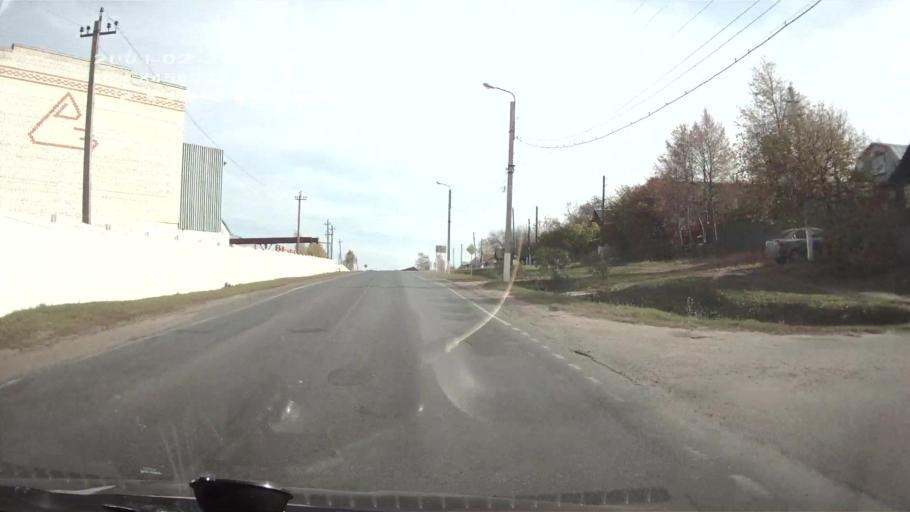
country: RU
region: Mordoviya
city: Turgenevo
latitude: 54.8457
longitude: 46.3420
